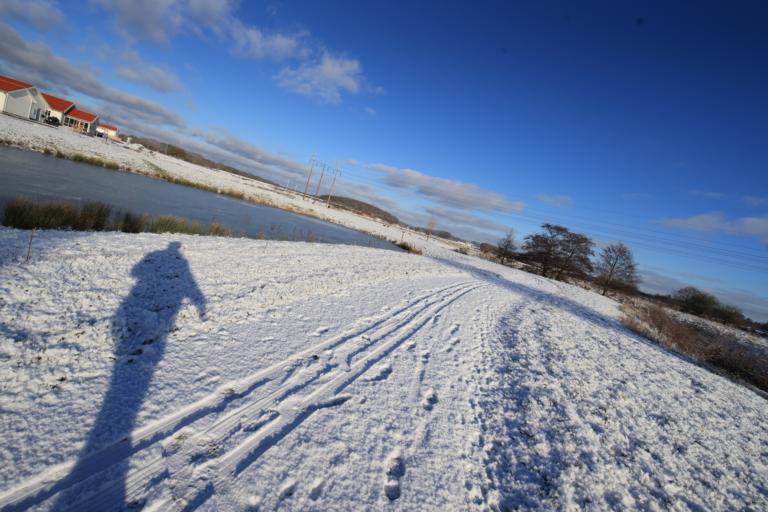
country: SE
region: Halland
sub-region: Varbergs Kommun
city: Varberg
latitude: 57.1339
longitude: 12.2994
